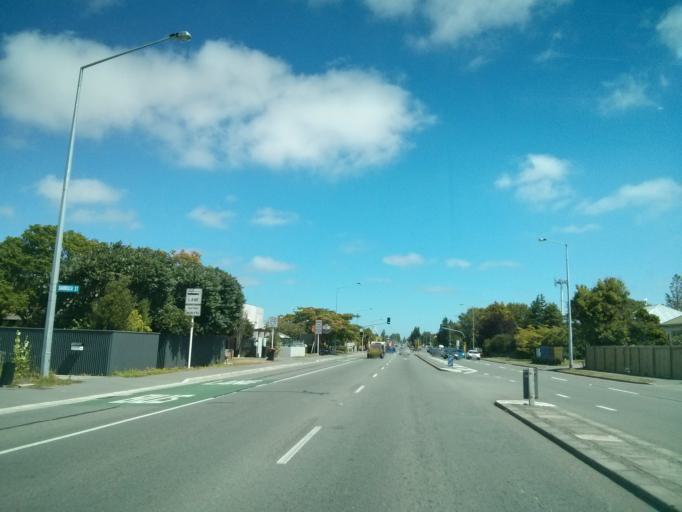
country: NZ
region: Canterbury
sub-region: Waimakariri District
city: Kaiapoi
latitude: -43.4438
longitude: 172.6333
